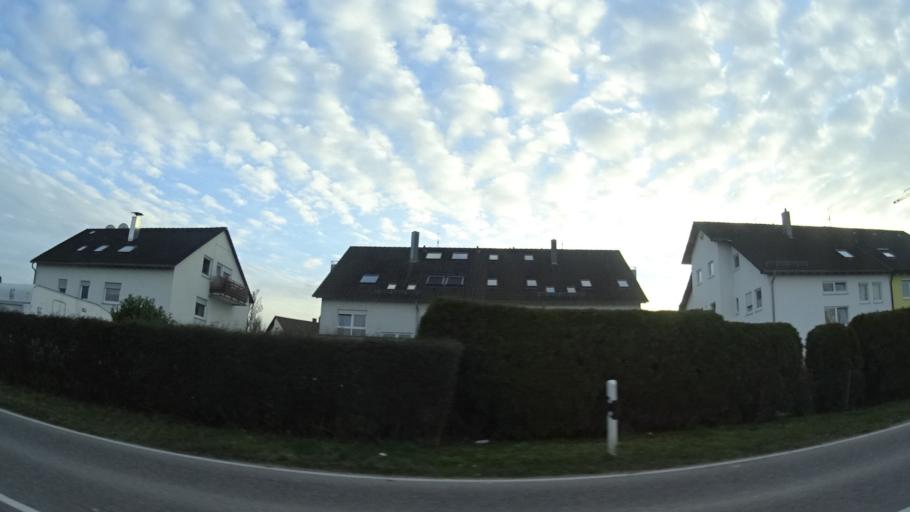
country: DE
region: Baden-Wuerttemberg
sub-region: Regierungsbezirk Stuttgart
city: Hemmingen
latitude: 48.8695
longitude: 9.0277
